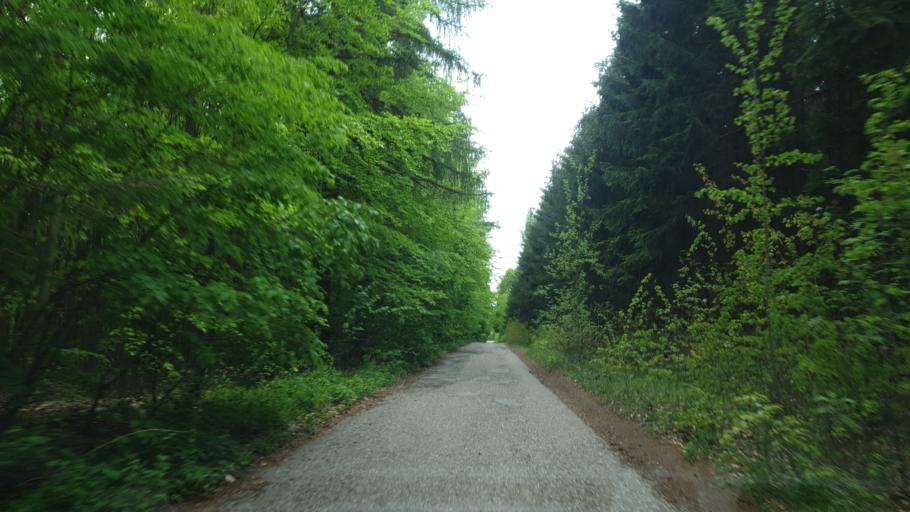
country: DE
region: Saxony
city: Hohndorf
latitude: 50.7196
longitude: 12.6647
